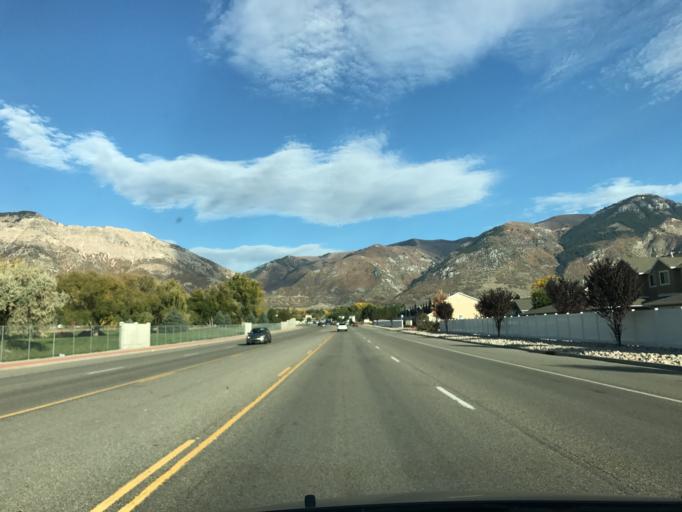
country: US
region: Utah
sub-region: Weber County
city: Pleasant View
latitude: 41.3056
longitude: -111.9835
